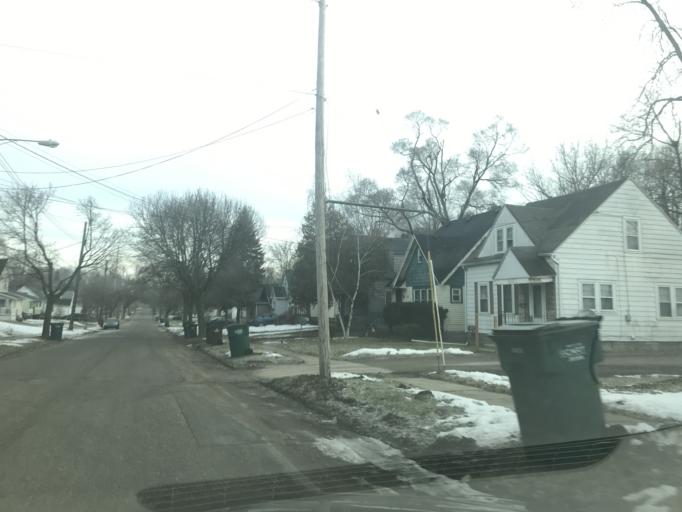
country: US
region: Michigan
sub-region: Ingham County
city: Lansing
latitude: 42.7512
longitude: -84.5691
